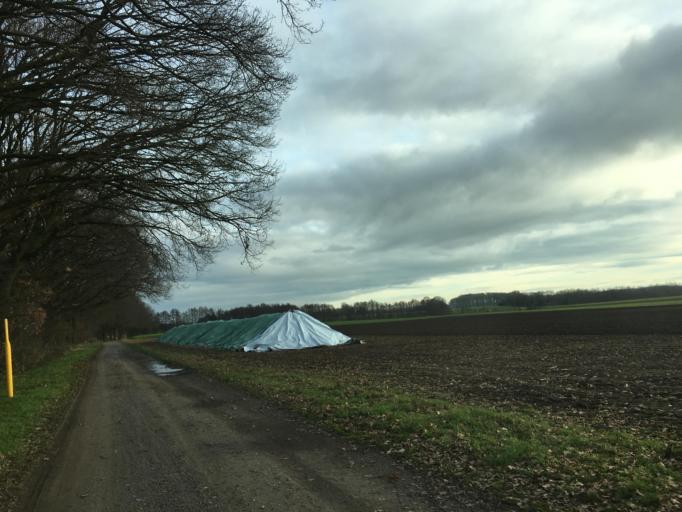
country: DE
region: North Rhine-Westphalia
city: Olfen
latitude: 51.7591
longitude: 7.3327
